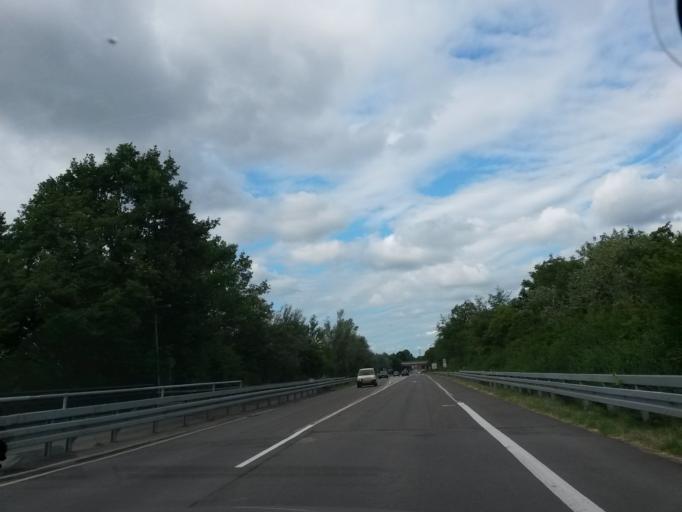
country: DE
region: Baden-Wuerttemberg
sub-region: Karlsruhe Region
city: Ettlingen
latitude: 48.9321
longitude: 8.3829
